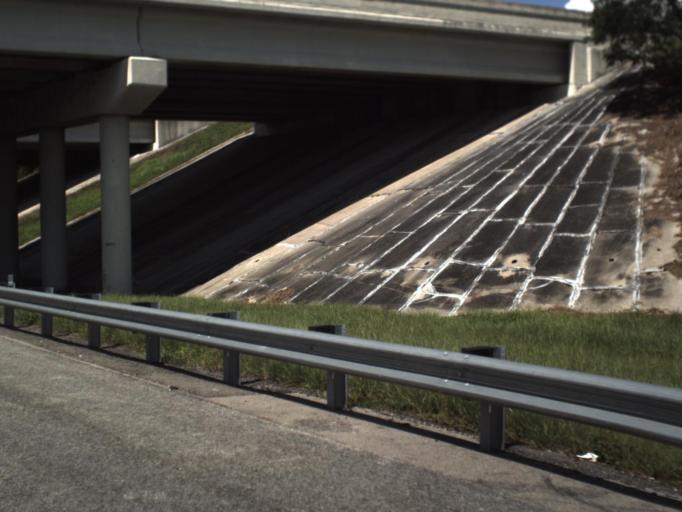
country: US
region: Florida
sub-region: Charlotte County
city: Punta Gorda
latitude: 26.9409
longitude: -82.0186
